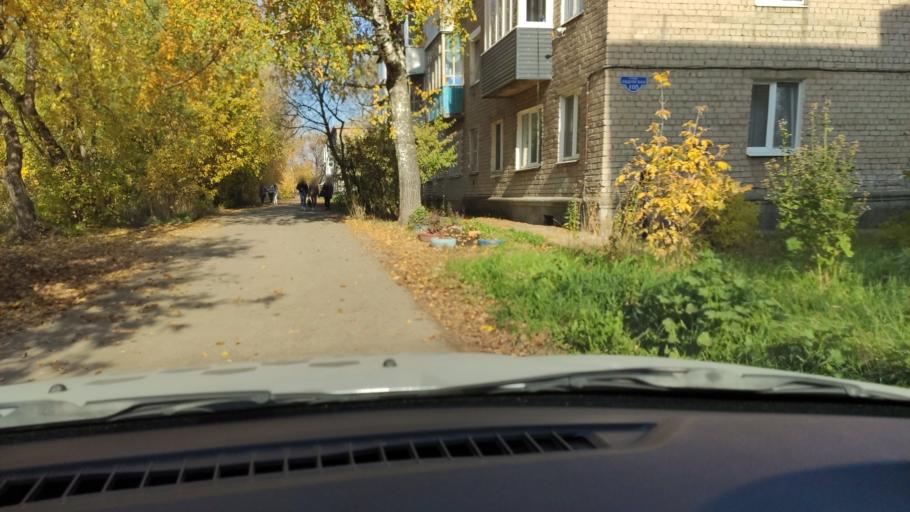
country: RU
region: Perm
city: Perm
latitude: 58.0369
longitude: 56.3537
